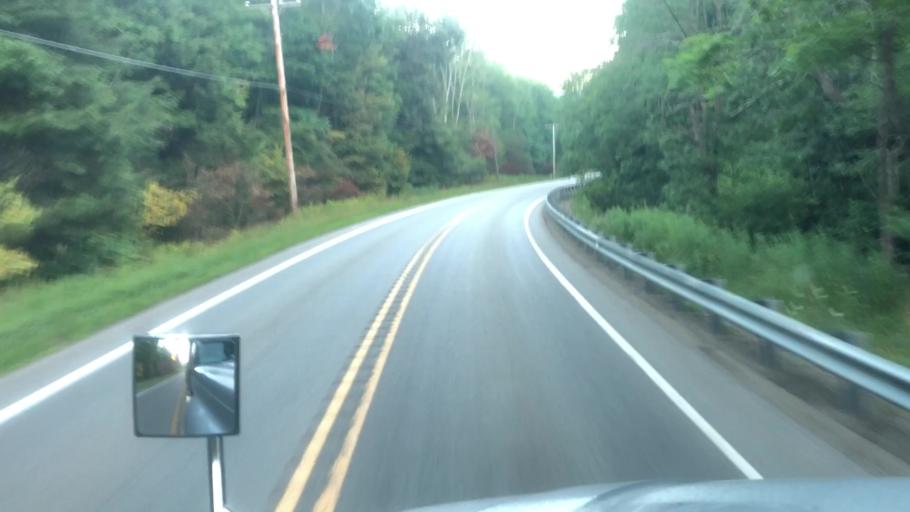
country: US
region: Pennsylvania
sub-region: Venango County
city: Hasson Heights
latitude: 41.4811
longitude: -79.6652
